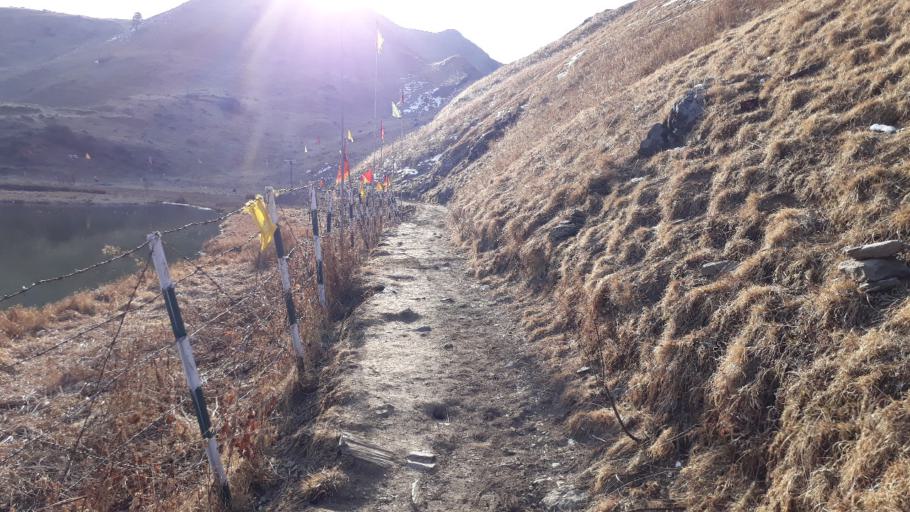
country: IN
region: Himachal Pradesh
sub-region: Mandi
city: Pandoh
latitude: 31.7543
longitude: 77.1007
